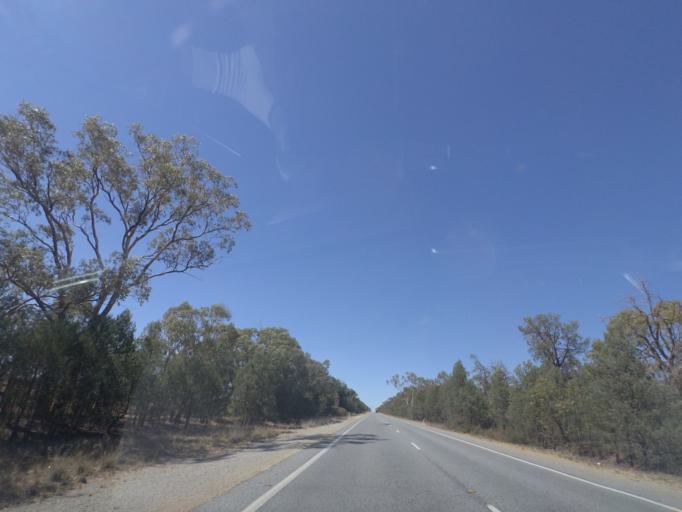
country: AU
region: New South Wales
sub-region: Narrandera
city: Narrandera
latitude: -34.4269
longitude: 146.8439
